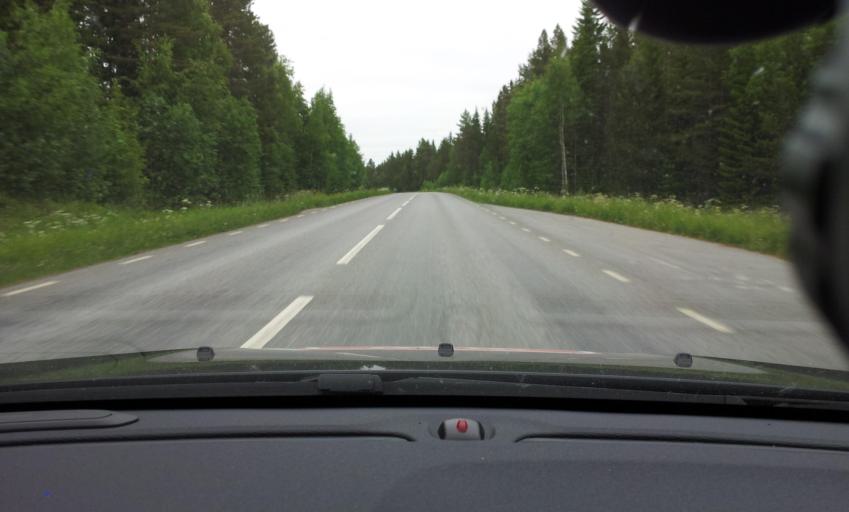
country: SE
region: Jaemtland
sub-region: Krokoms Kommun
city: Valla
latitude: 63.2131
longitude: 14.0260
